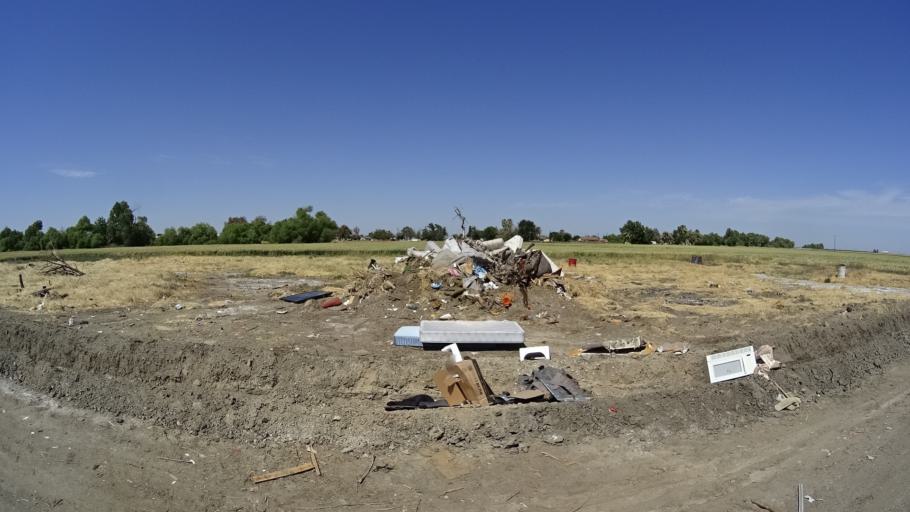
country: US
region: California
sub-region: Kings County
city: Stratford
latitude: 36.1946
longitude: -119.8160
